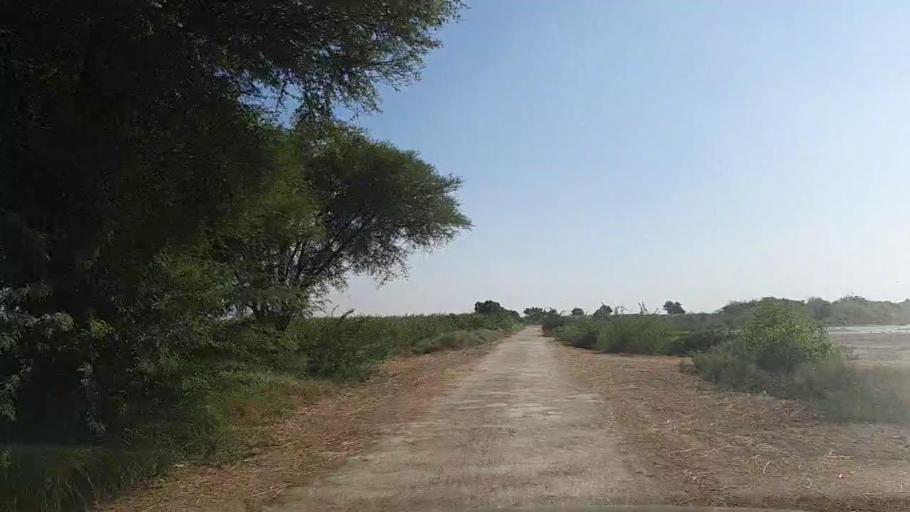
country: PK
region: Sindh
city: Daro Mehar
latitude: 24.7699
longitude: 68.0692
